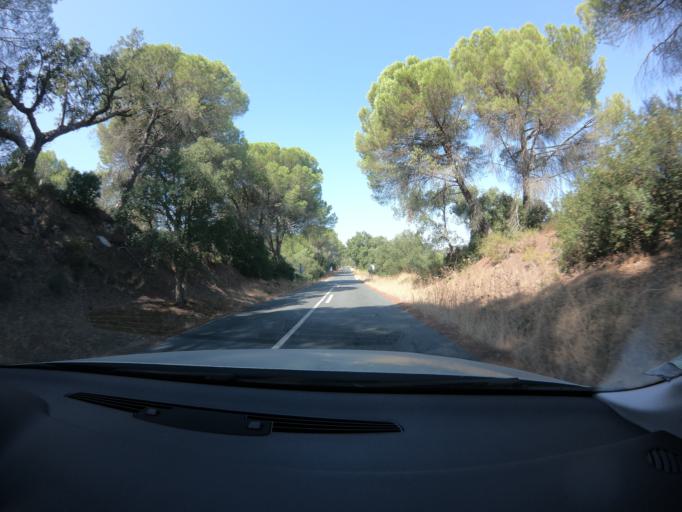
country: PT
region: Setubal
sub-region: Alcacer do Sal
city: Alcacer do Sal
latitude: 38.3045
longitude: -8.4187
